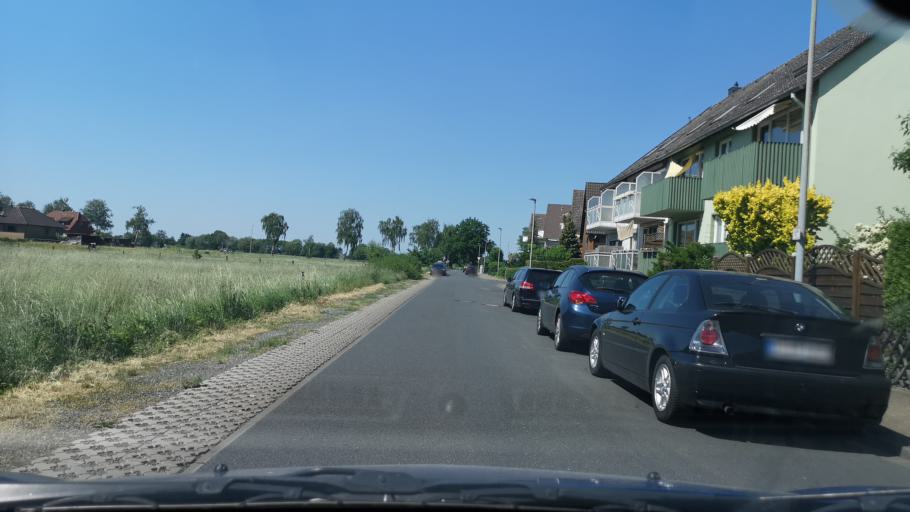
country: DE
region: Lower Saxony
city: Garbsen-Mitte
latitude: 52.4491
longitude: 9.6141
